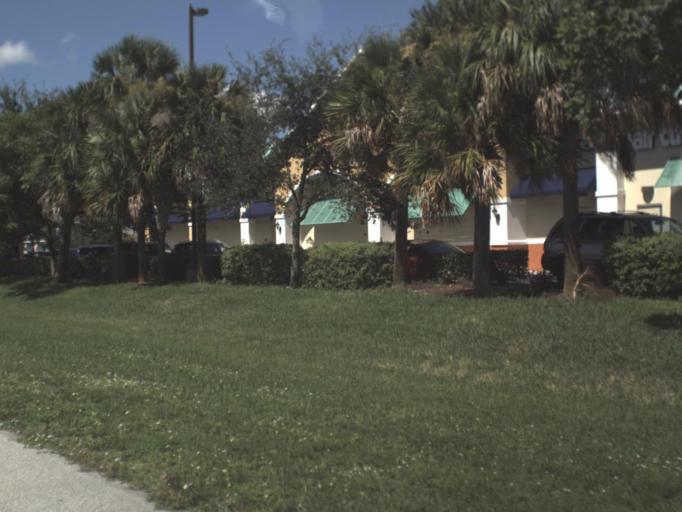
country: US
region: Florida
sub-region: Lee County
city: Cape Coral
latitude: 26.6074
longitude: -82.0259
